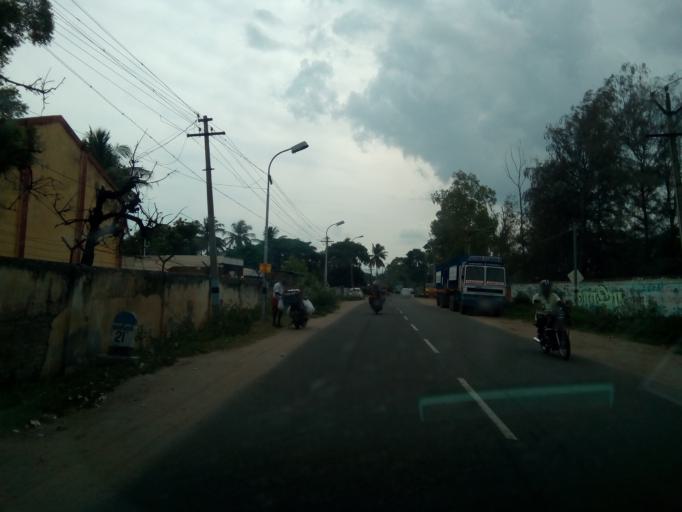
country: IN
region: Tamil Nadu
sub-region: Coimbatore
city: Coimbatore
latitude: 11.0061
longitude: 76.9376
